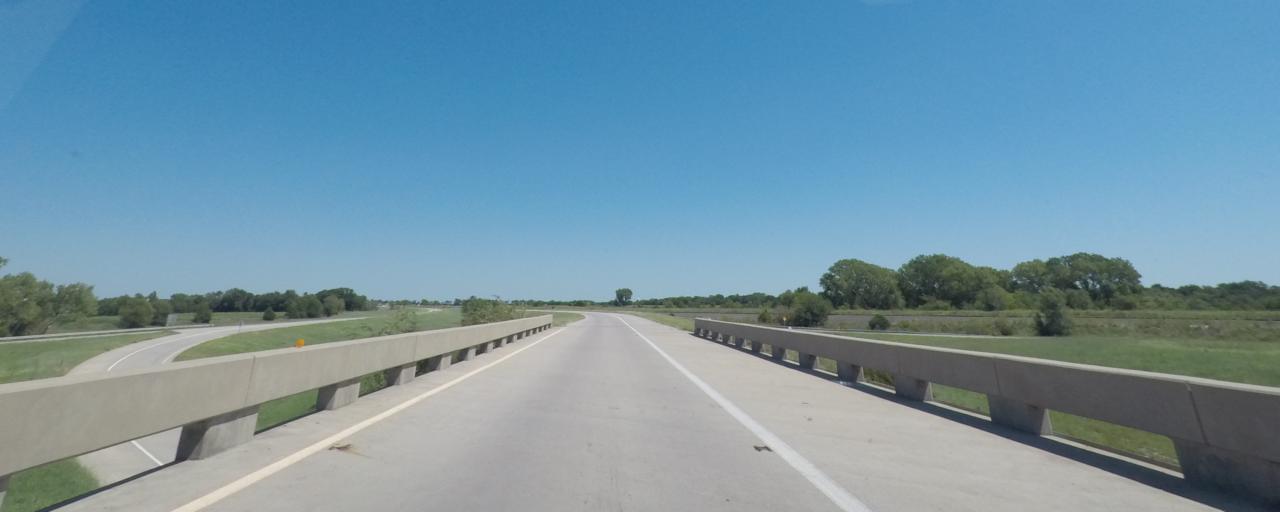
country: US
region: Kansas
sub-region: Harvey County
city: North Newton
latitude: 38.0666
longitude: -97.3137
